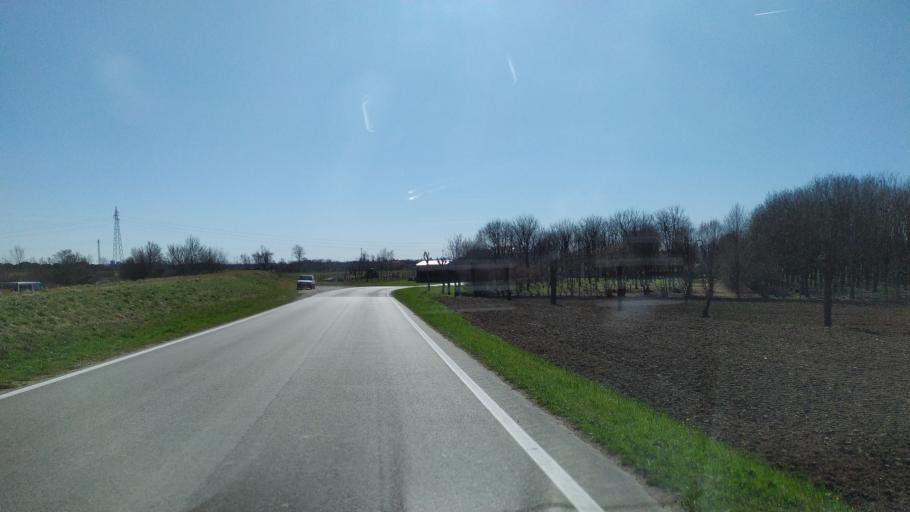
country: IT
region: Veneto
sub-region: Provincia di Vicenza
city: Sandrigo
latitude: 45.6363
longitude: 11.6013
